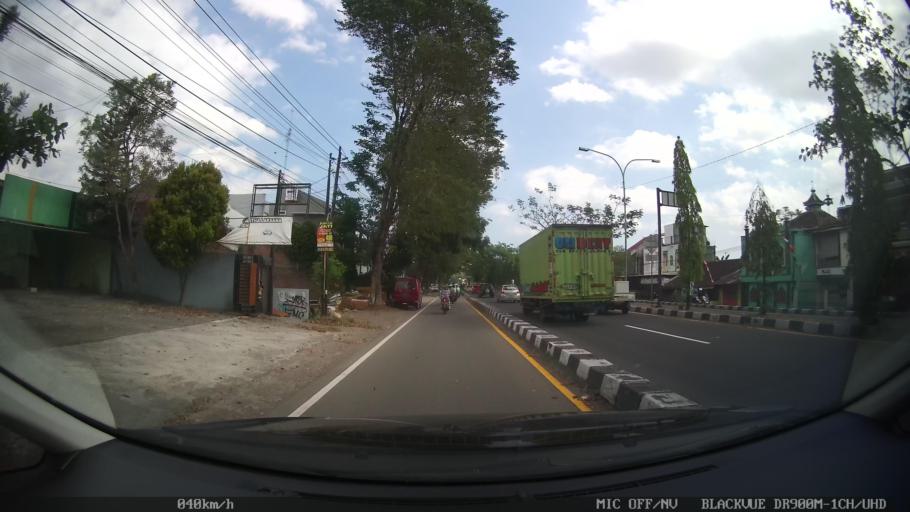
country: ID
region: Daerah Istimewa Yogyakarta
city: Gamping Lor
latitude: -7.7742
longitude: 110.3328
